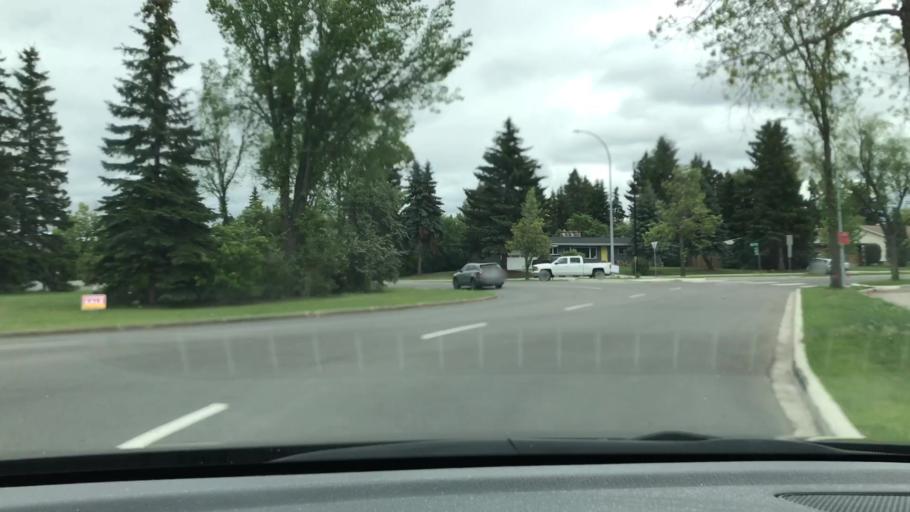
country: CA
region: Alberta
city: Edmonton
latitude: 53.5193
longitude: -113.5664
